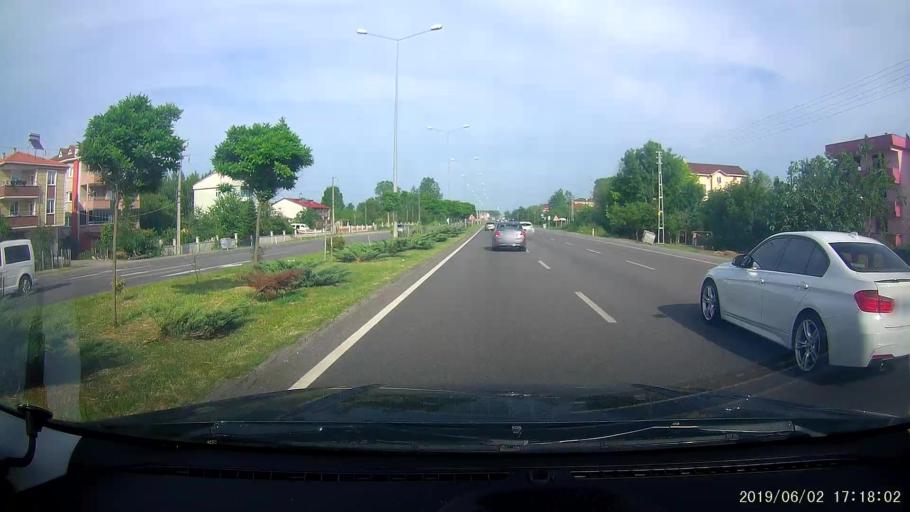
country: TR
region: Samsun
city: Dikbiyik
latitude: 41.2257
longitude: 36.5912
